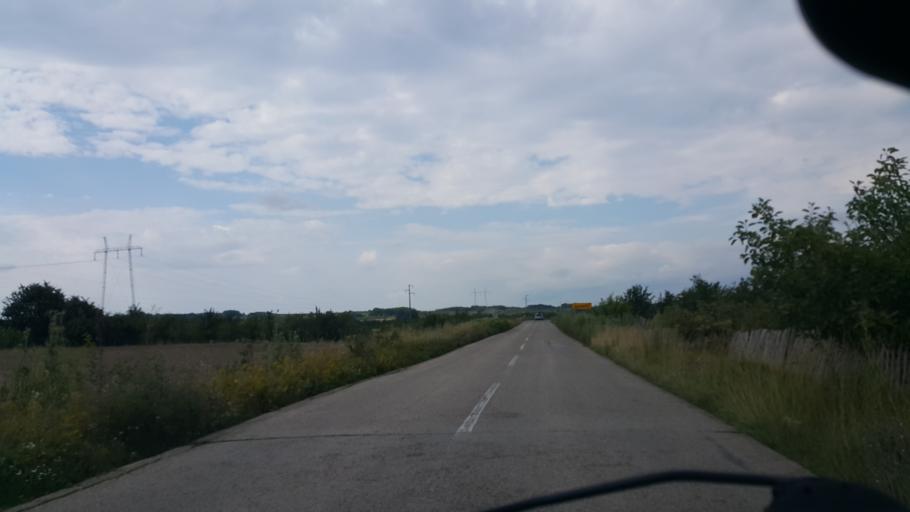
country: RS
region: Central Serbia
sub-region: Toplicki Okrug
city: Blace
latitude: 43.2405
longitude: 21.2570
